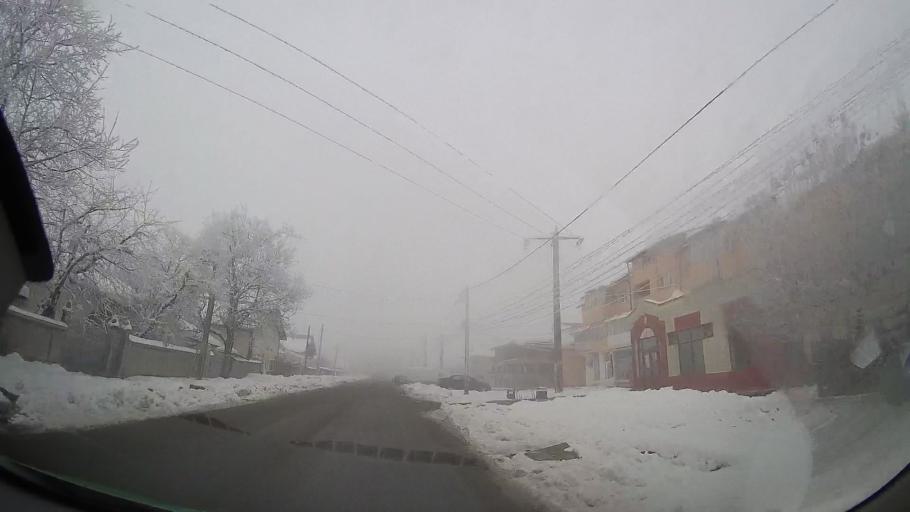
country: RO
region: Neamt
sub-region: Comuna Sabaoani
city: Sabaoani
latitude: 47.0180
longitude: 26.8657
